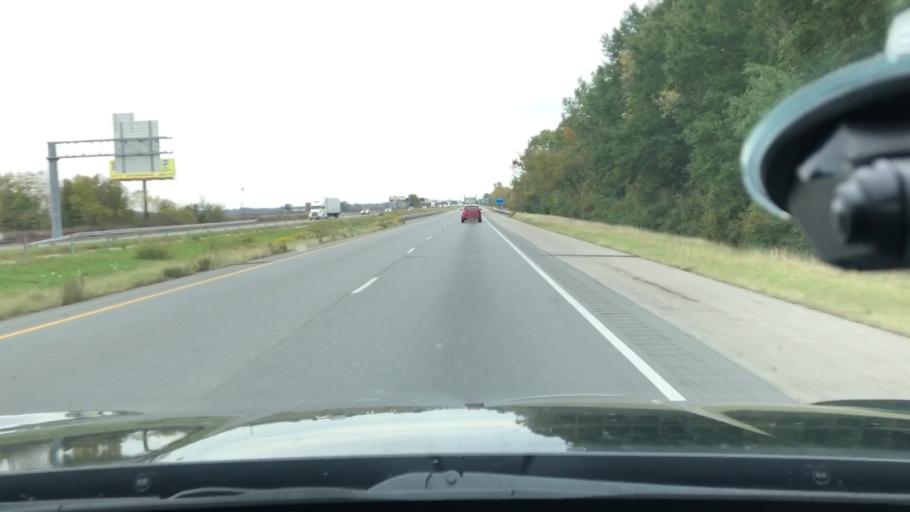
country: US
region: Arkansas
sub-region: Miller County
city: Texarkana
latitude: 33.4926
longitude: -93.9674
